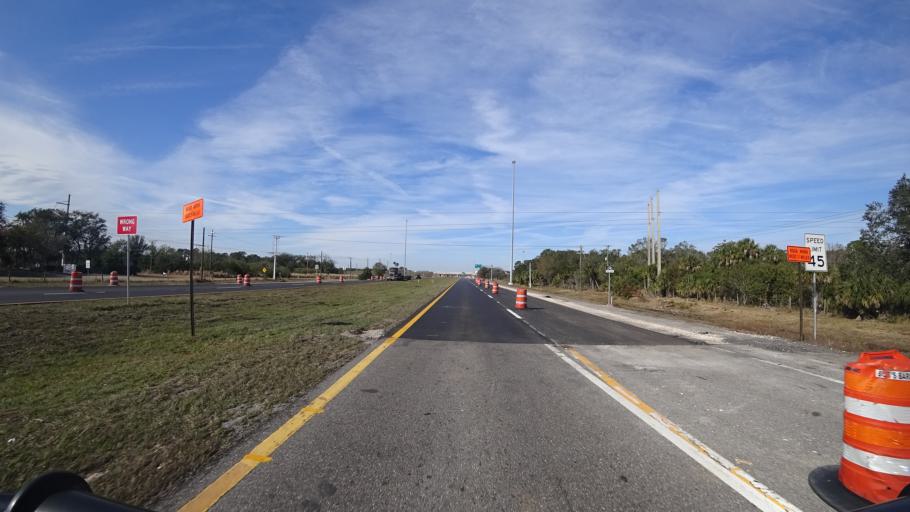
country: US
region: Florida
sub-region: Manatee County
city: Ellenton
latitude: 27.6013
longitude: -82.4972
